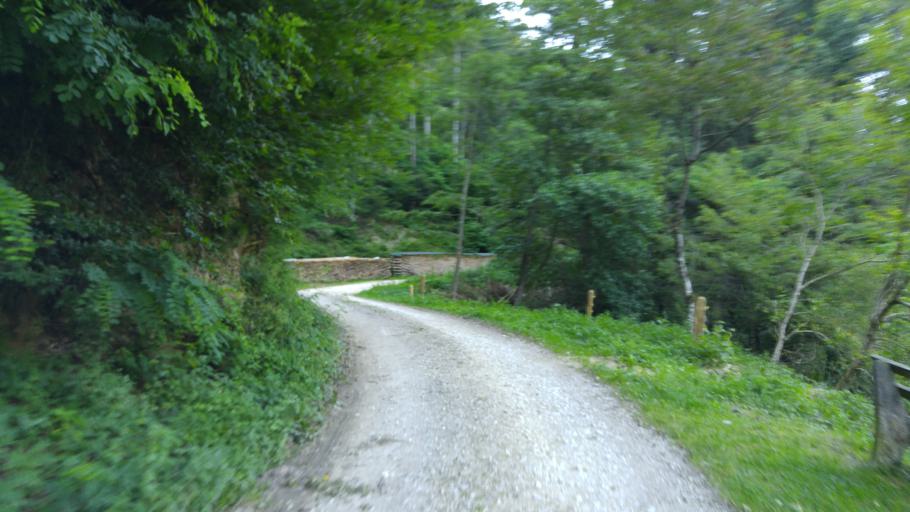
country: DE
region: Baden-Wuerttemberg
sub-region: Freiburg Region
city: Muenstertal/Schwarzwald
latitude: 47.8371
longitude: 7.7870
